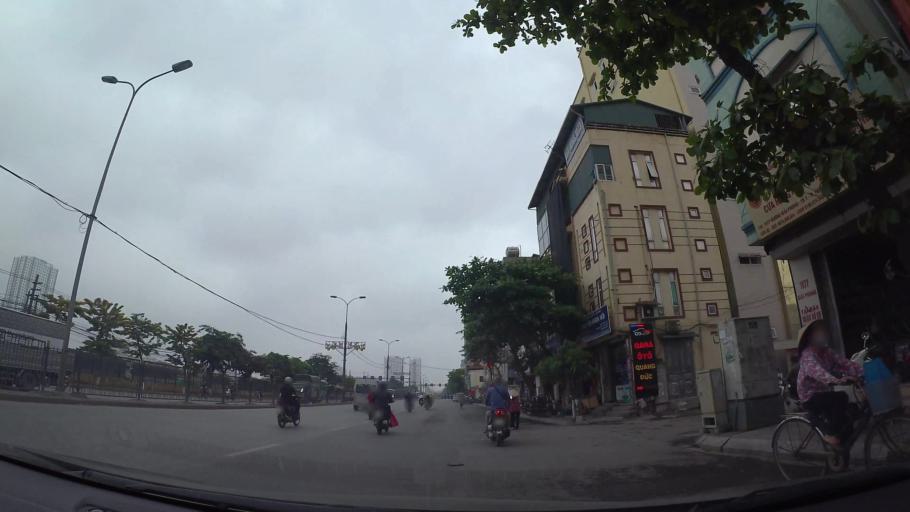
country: VN
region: Ha Noi
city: Van Dien
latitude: 20.9754
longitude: 105.8410
